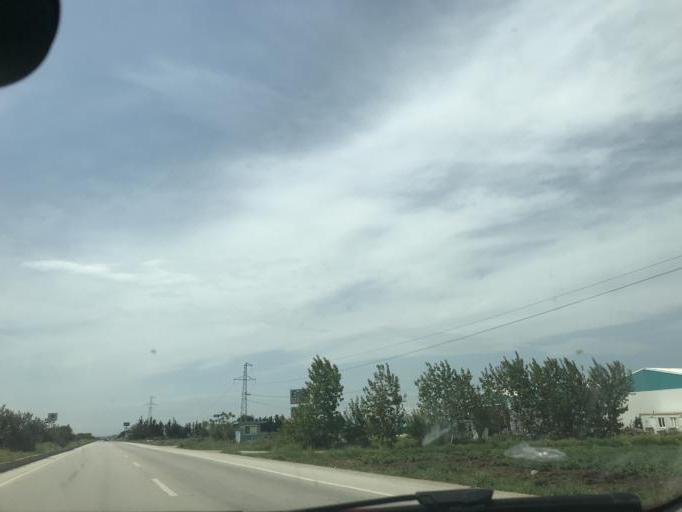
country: TR
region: Adana
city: Yakapinar
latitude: 36.9747
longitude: 35.4952
